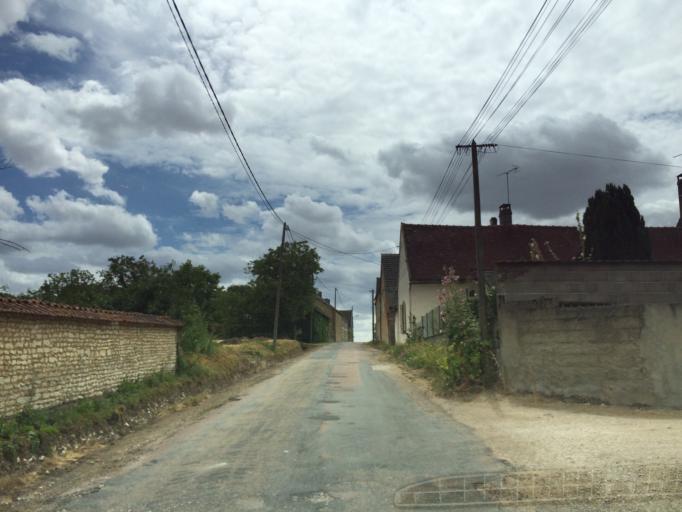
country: FR
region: Bourgogne
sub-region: Departement de l'Yonne
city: Fleury-la-Vallee
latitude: 47.8579
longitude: 3.4076
